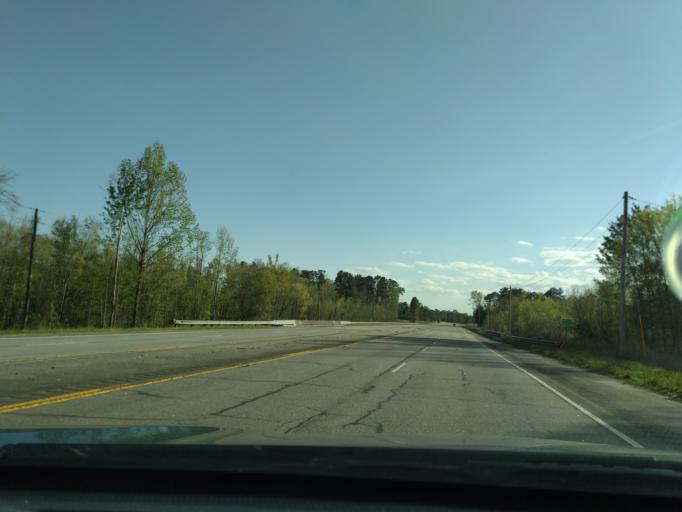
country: US
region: South Carolina
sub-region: Williamsburg County
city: Kingstree
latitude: 33.6241
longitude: -79.9259
